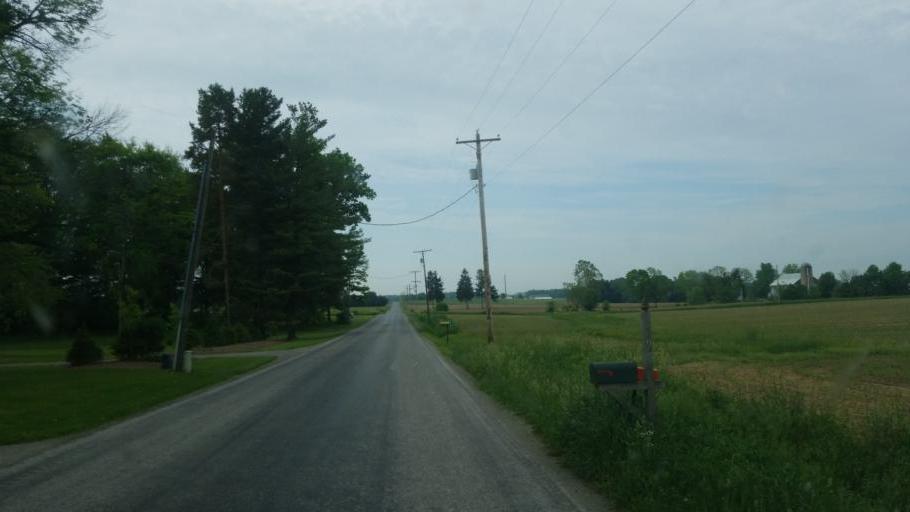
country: US
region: Ohio
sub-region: Wayne County
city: Dalton
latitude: 40.7648
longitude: -81.7550
